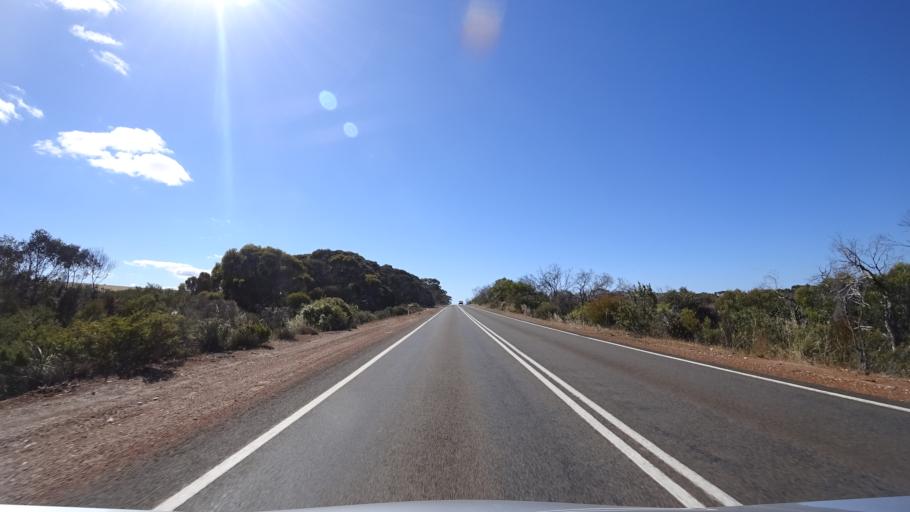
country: AU
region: South Australia
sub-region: Kangaroo Island
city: Kingscote
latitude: -35.7636
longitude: 137.6134
